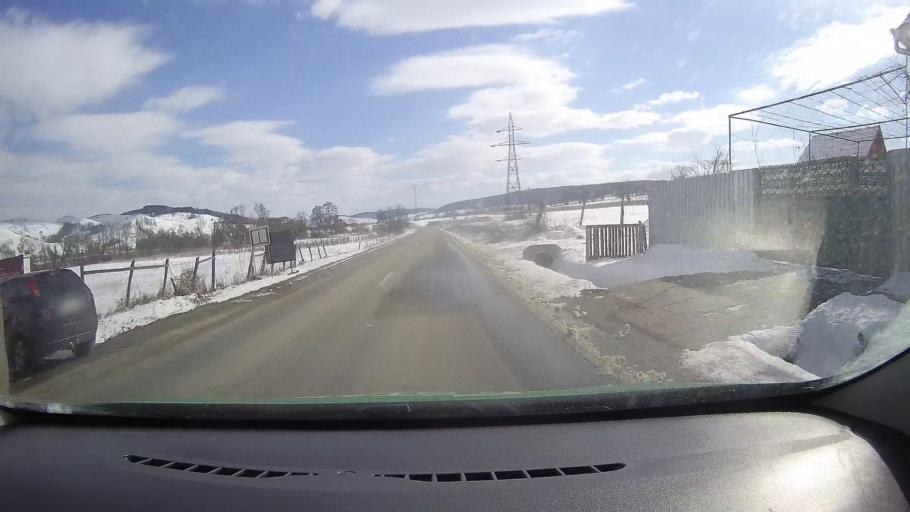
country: RO
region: Sibiu
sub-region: Comuna Barghis
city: Barghis
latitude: 45.9793
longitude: 24.5409
